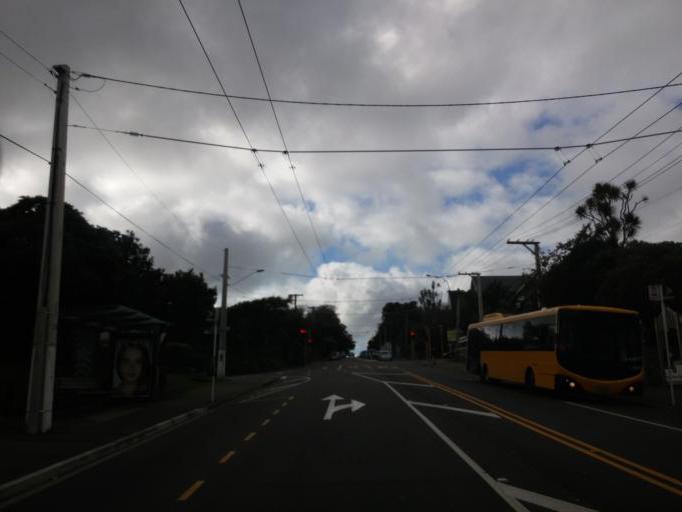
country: NZ
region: Wellington
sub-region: Wellington City
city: Kelburn
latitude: -41.2838
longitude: 174.7408
